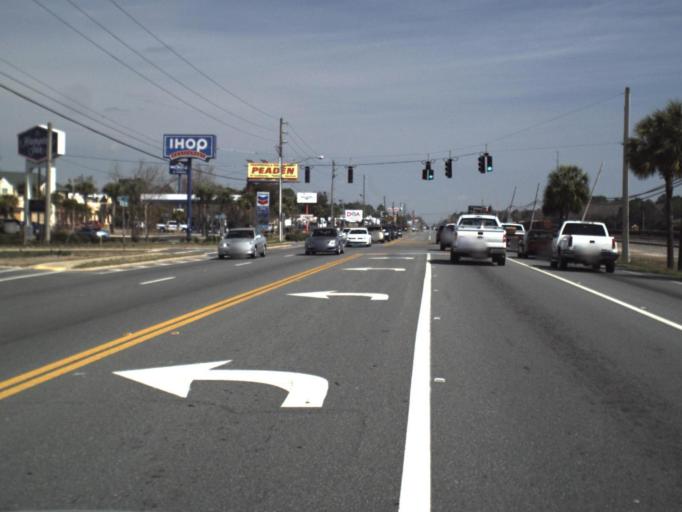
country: US
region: Florida
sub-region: Bay County
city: Hiland Park
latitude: 30.1890
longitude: -85.6415
